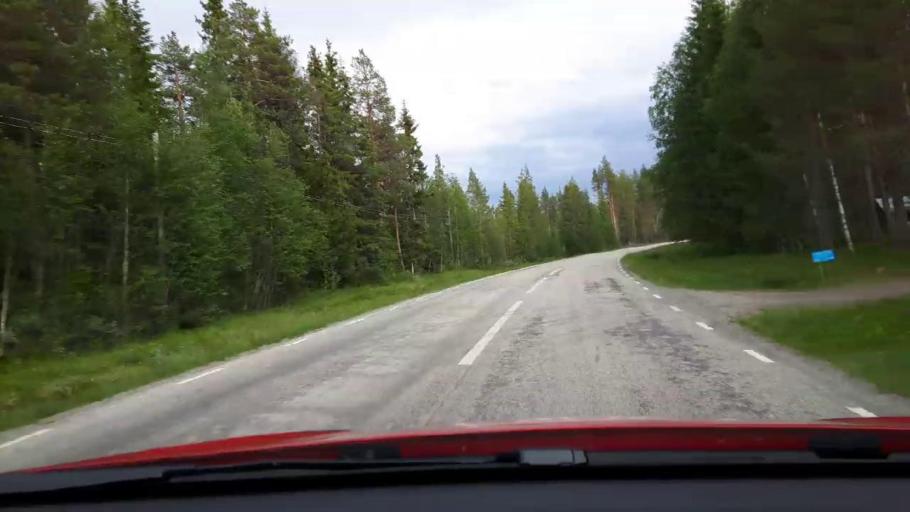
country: SE
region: Jaemtland
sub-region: Bergs Kommun
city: Hoverberg
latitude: 62.6626
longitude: 14.0521
